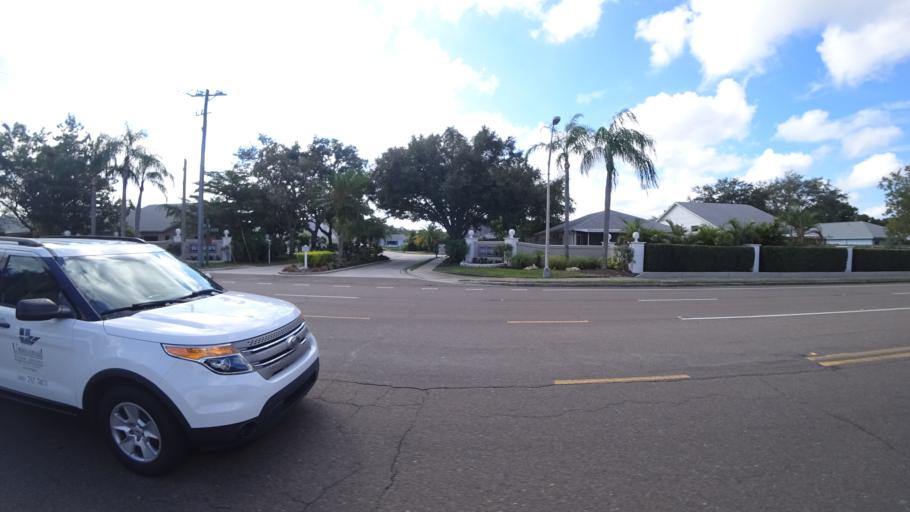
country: US
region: Florida
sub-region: Sarasota County
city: North Sarasota
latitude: 27.4035
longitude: -82.5094
